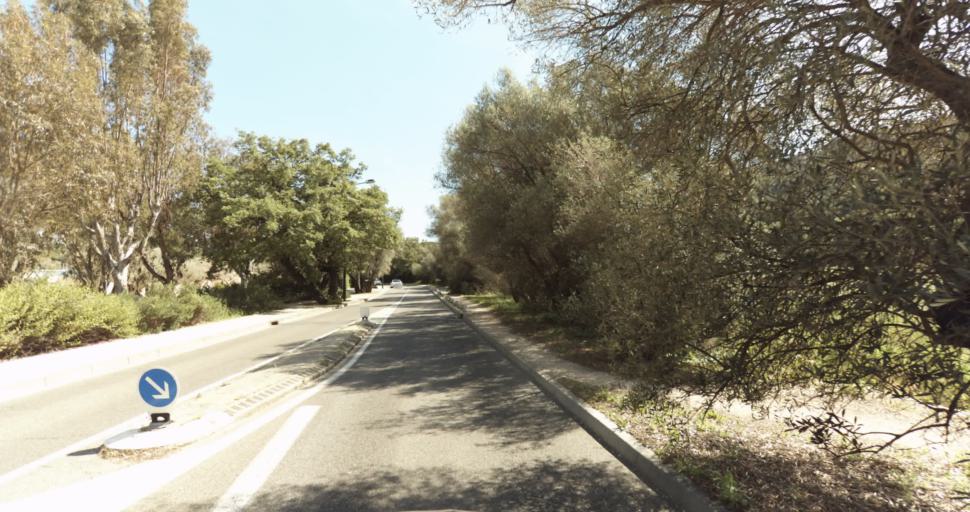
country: FR
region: Provence-Alpes-Cote d'Azur
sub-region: Departement du Var
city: Hyeres
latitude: 43.0992
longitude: 6.1213
